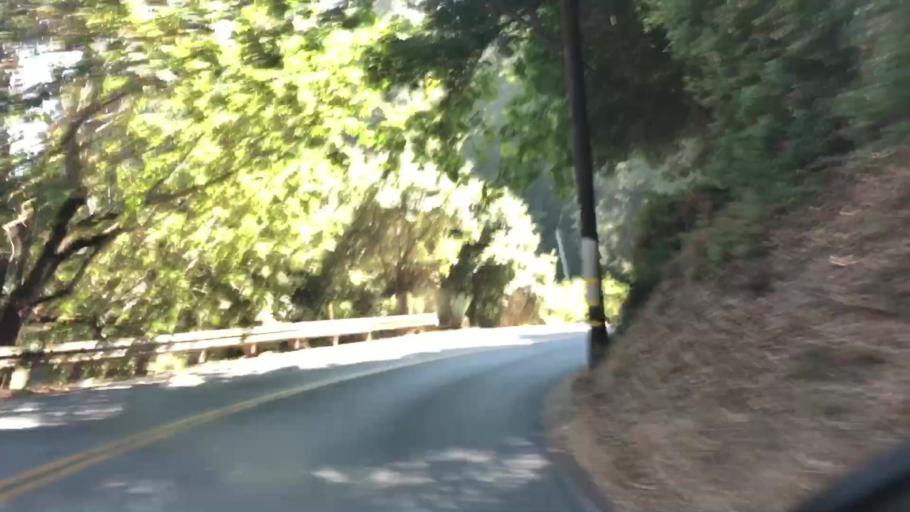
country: US
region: California
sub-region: Santa Cruz County
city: Corralitos
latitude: 37.0071
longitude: -121.8093
